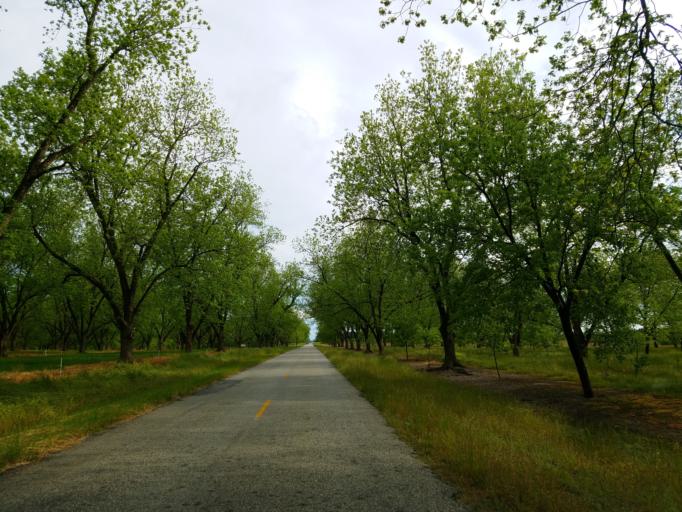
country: US
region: Georgia
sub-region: Dooly County
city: Vienna
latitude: 32.1594
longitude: -83.7607
